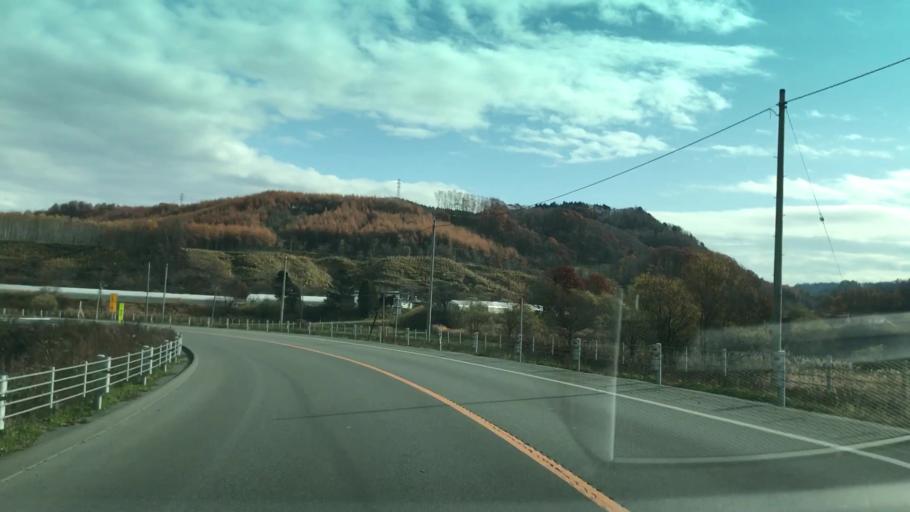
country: JP
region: Hokkaido
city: Shizunai-furukawacho
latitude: 42.7251
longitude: 142.3138
